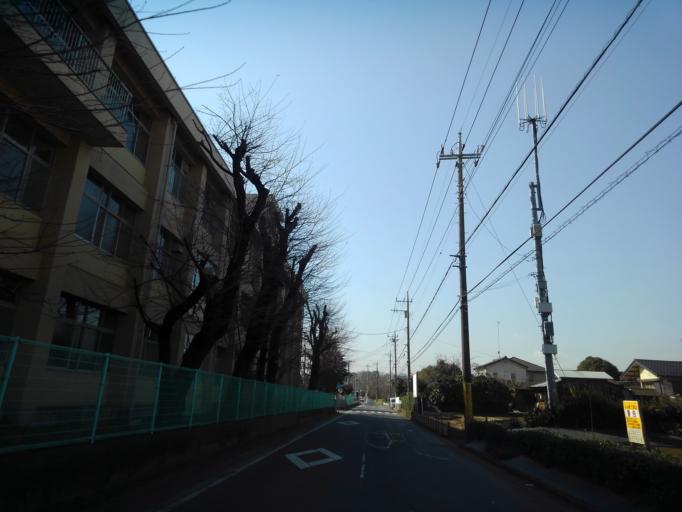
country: JP
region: Saitama
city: Tokorozawa
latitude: 35.7967
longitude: 139.4959
